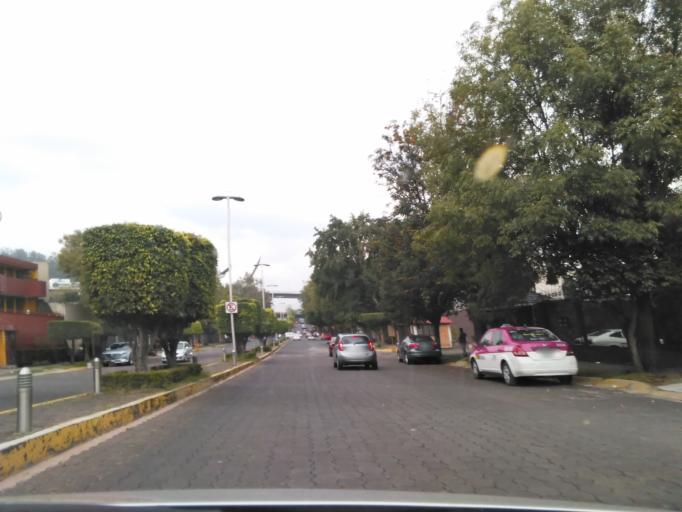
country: MX
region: Mexico City
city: Tlalpan
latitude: 19.2986
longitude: -99.1925
